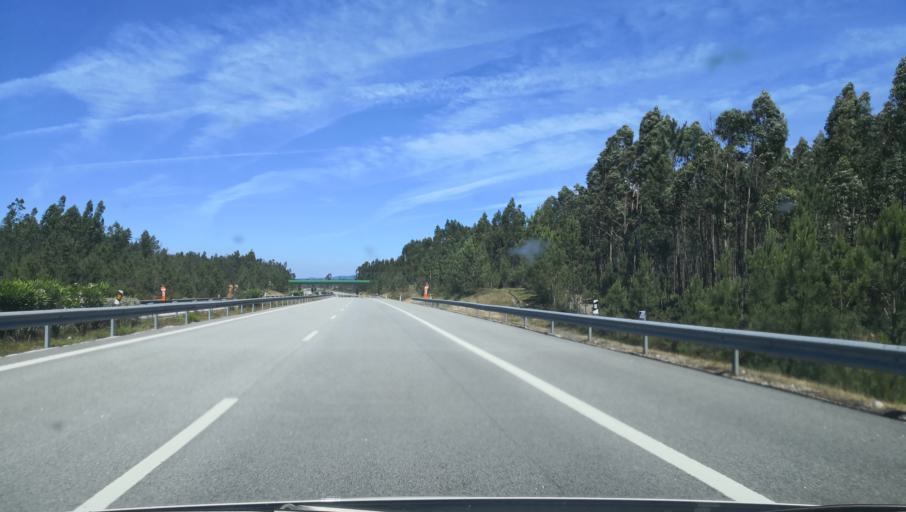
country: PT
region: Coimbra
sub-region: Montemor-O-Velho
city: Arazede
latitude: 40.2753
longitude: -8.5940
